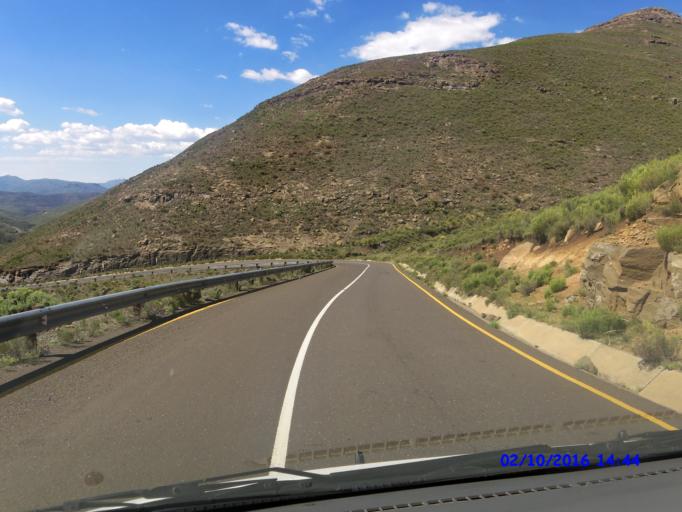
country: LS
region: Maseru
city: Nako
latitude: -29.5234
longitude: 28.0612
